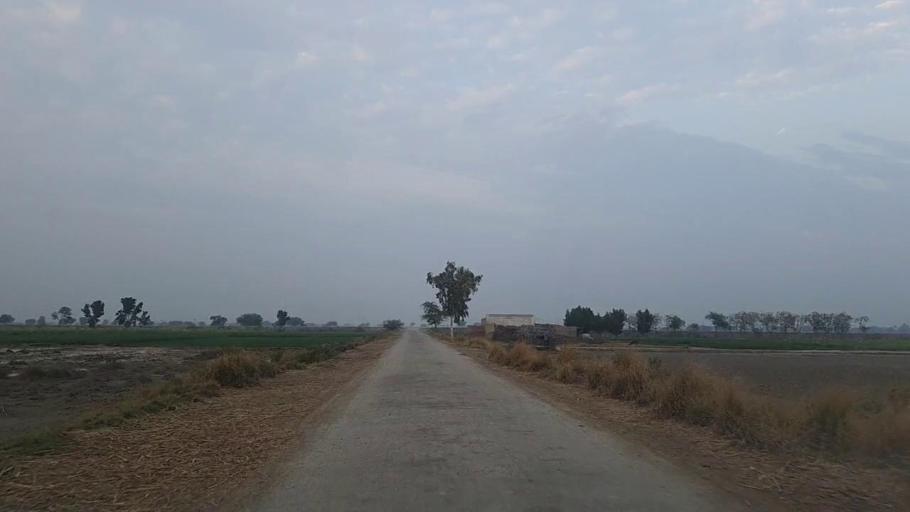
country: PK
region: Sindh
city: Jam Sahib
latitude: 26.3067
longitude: 68.5937
